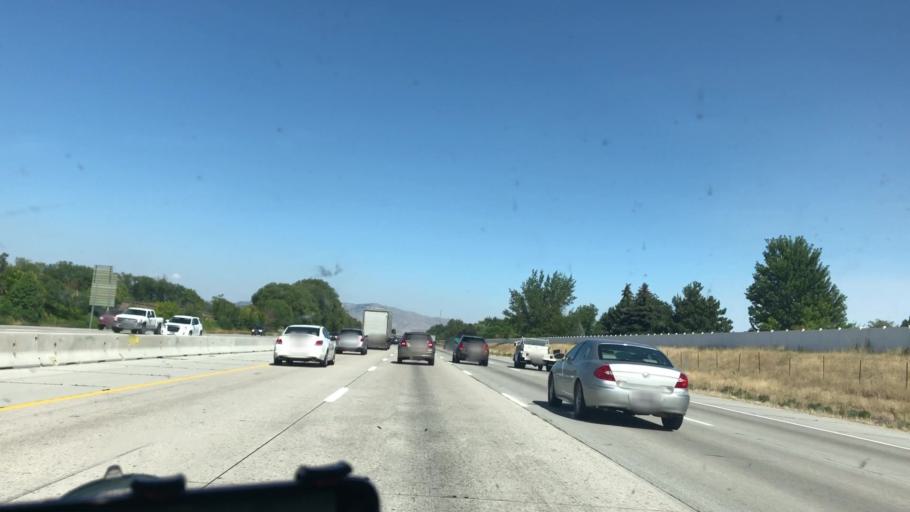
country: US
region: Idaho
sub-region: Ada County
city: Meridian
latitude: 43.5972
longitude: -116.3280
